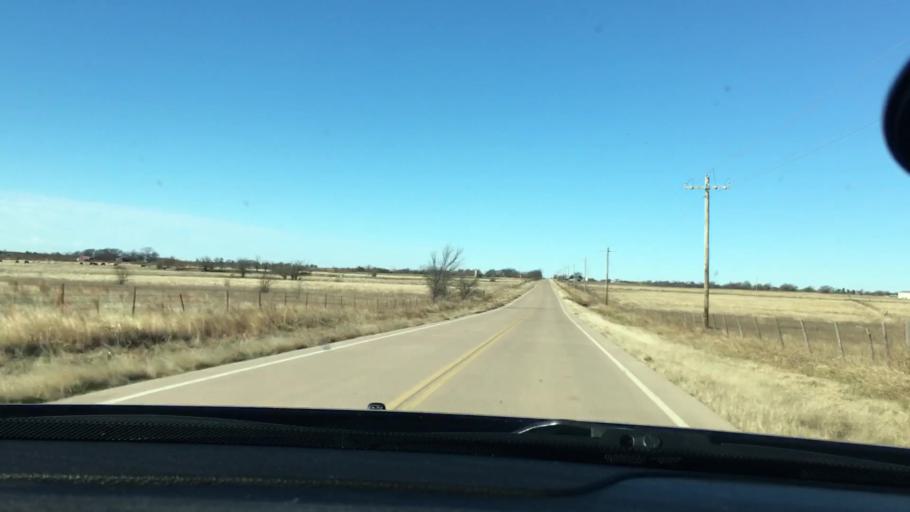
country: US
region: Oklahoma
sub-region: Marshall County
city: Madill
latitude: 34.1145
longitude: -96.6958
